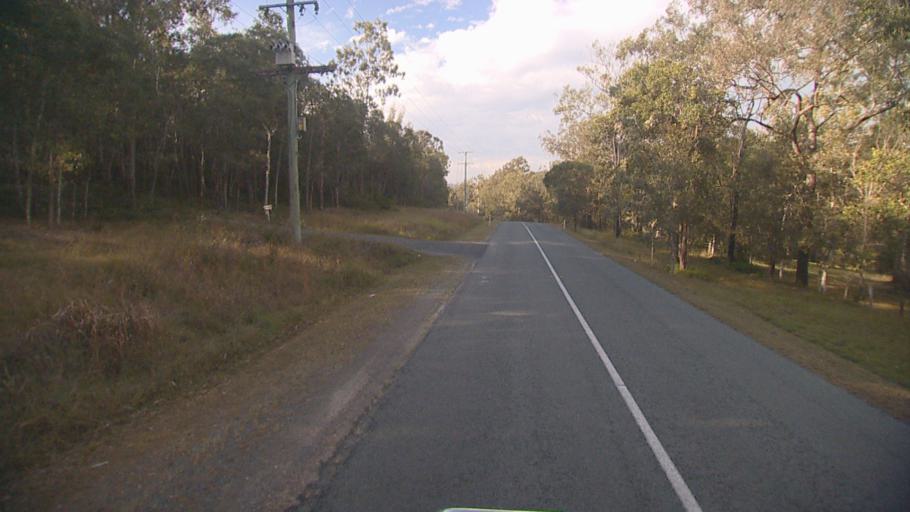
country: AU
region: Queensland
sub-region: Gold Coast
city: Ormeau Hills
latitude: -27.8393
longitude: 153.1660
